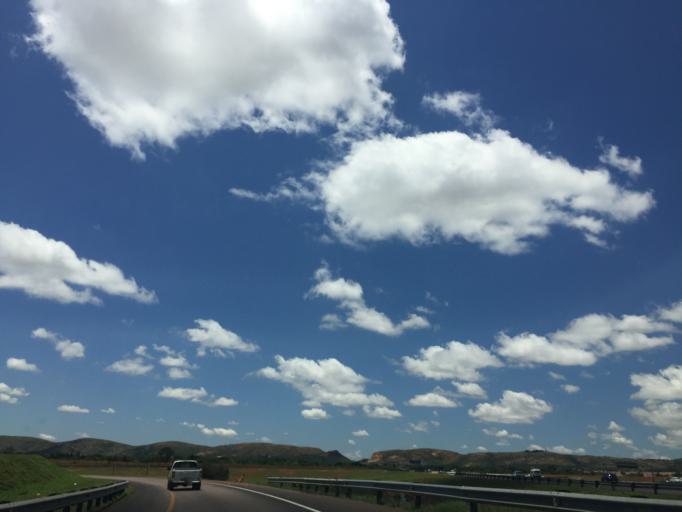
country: ZA
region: Gauteng
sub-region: City of Tshwane Metropolitan Municipality
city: Pretoria
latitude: -25.6511
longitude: 28.1139
